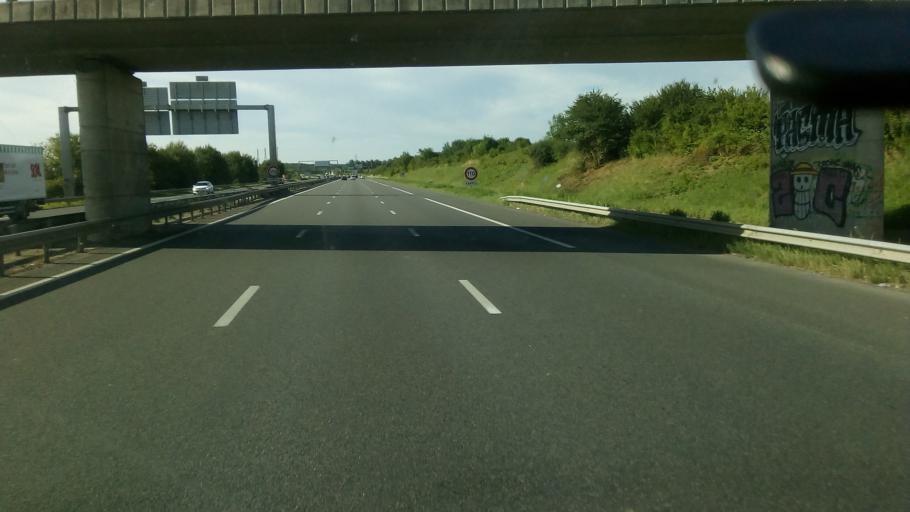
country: FR
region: Ile-de-France
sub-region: Departement de Seine-et-Marne
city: Vert-Saint-Denis
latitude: 48.5829
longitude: 2.6373
